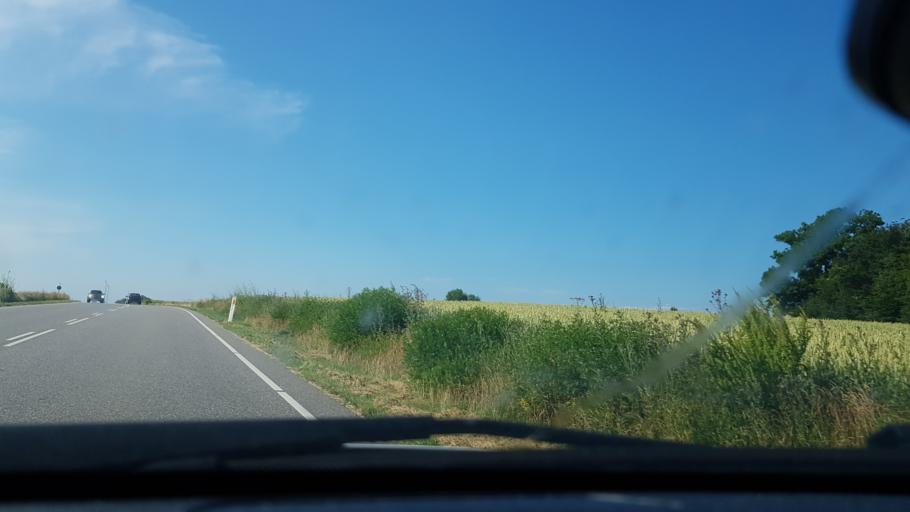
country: DK
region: Zealand
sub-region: Odsherred Kommune
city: Hojby
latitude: 55.8550
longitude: 11.5924
